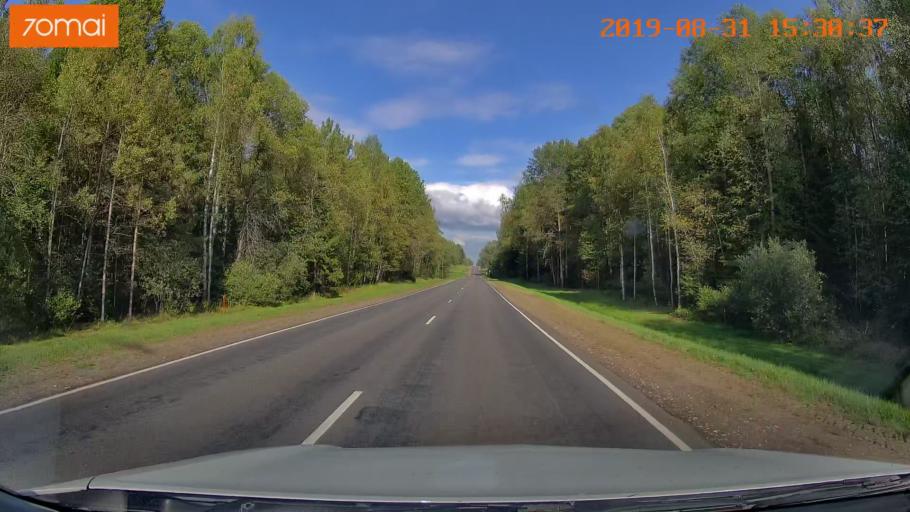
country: RU
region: Kaluga
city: Baryatino
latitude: 54.5769
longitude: 34.6345
